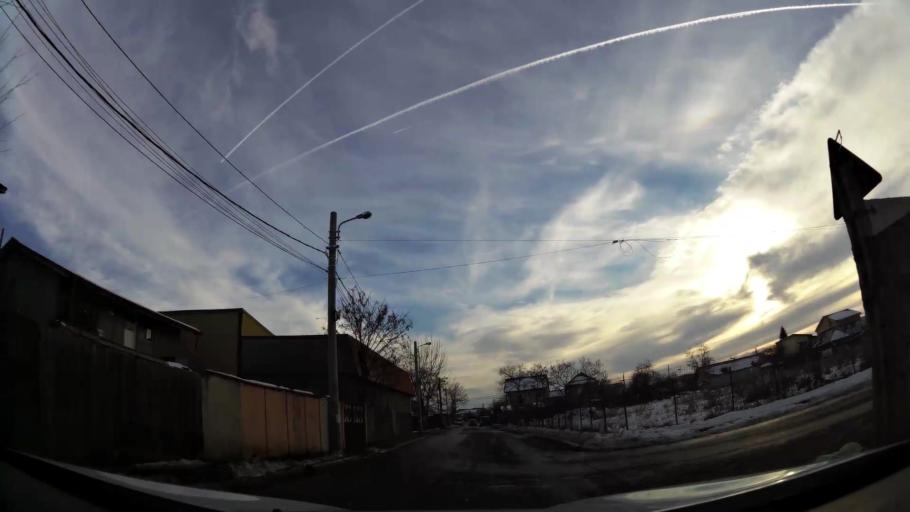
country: RO
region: Bucuresti
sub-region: Municipiul Bucuresti
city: Bucuresti
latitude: 44.3918
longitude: 26.0697
